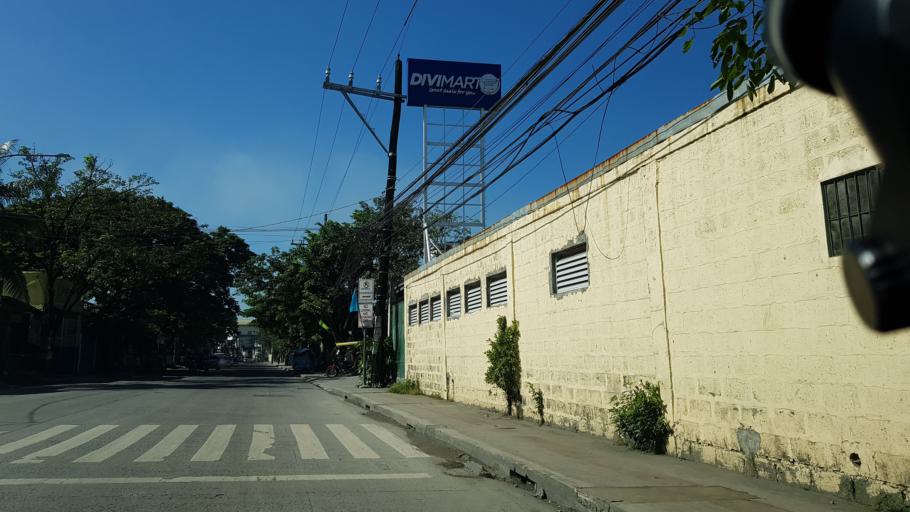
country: PH
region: Calabarzon
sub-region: Province of Rizal
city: Cainta
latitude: 14.5653
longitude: 121.0940
